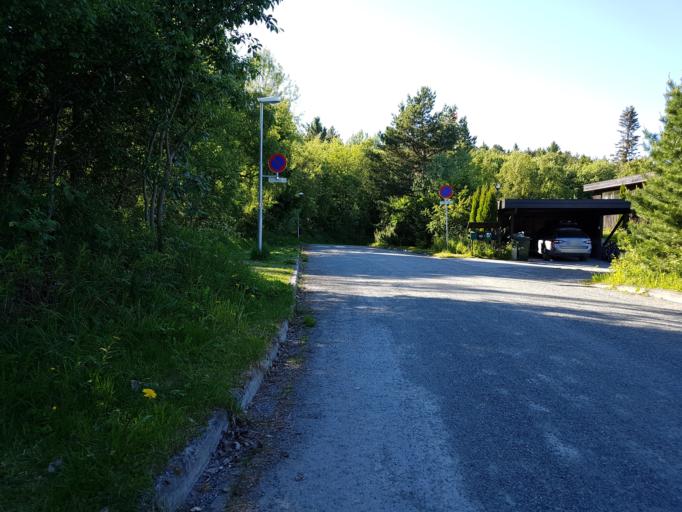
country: NO
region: Sor-Trondelag
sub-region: Trondheim
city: Trondheim
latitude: 63.4201
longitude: 10.3655
